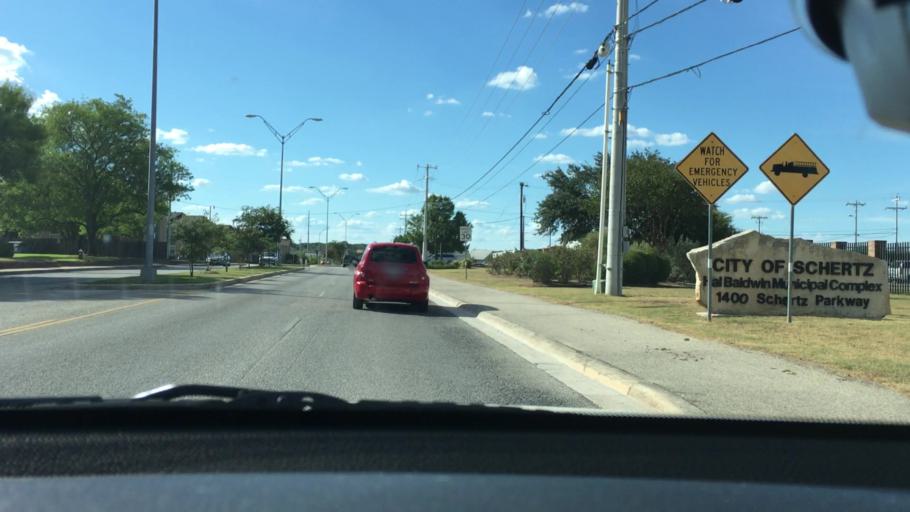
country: US
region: Texas
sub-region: Guadalupe County
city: Schertz
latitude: 29.5651
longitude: -98.2701
